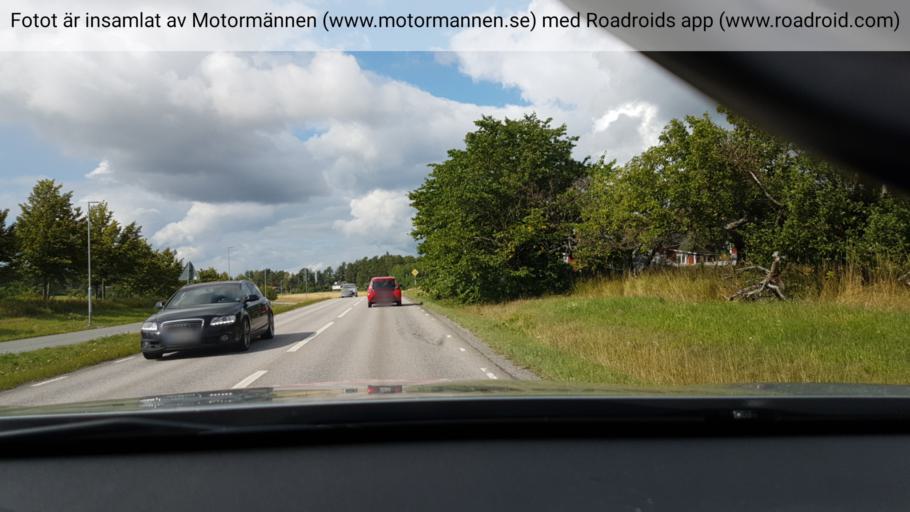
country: SE
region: Stockholm
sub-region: Ekero Kommun
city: Ekeroe
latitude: 59.3163
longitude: 17.7707
